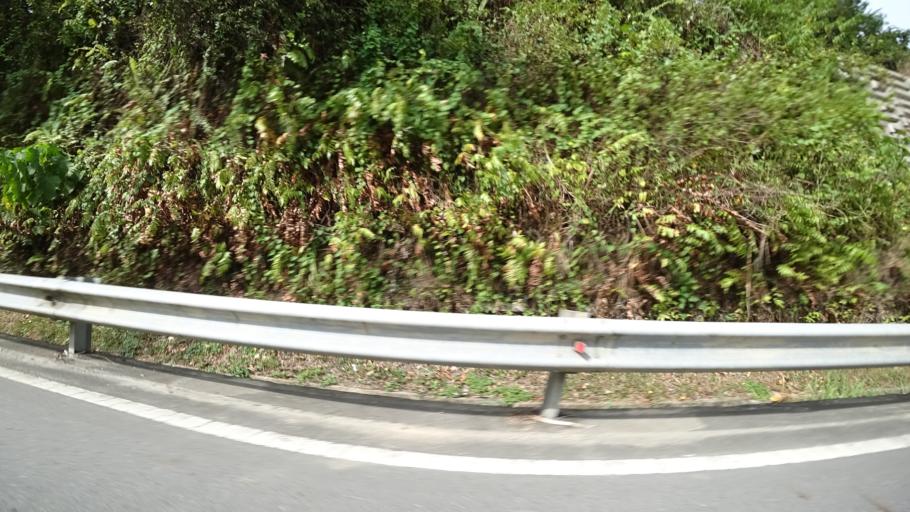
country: BN
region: Brunei and Muara
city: Bandar Seri Begawan
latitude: 4.8566
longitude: 114.8695
